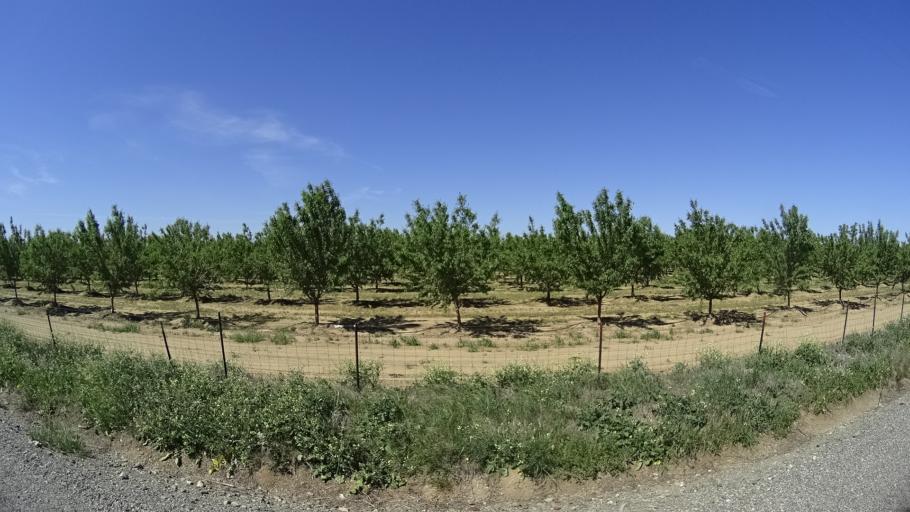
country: US
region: California
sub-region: Glenn County
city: Orland
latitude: 39.6639
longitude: -122.1406
